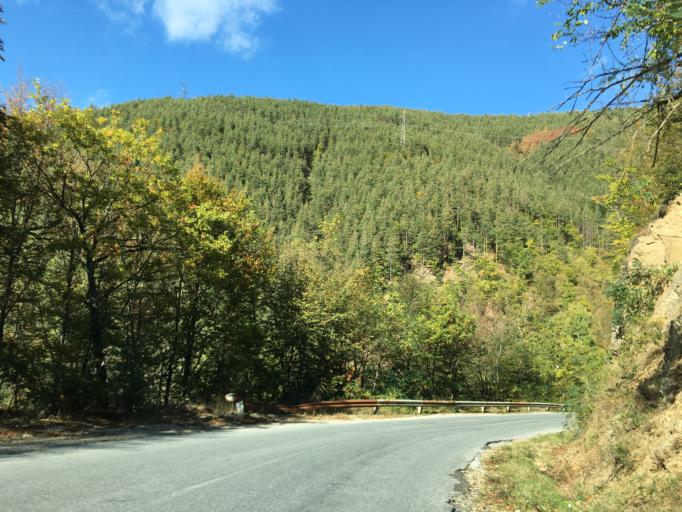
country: BG
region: Smolyan
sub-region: Obshtina Madan
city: Madan
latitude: 41.4563
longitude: 24.9806
